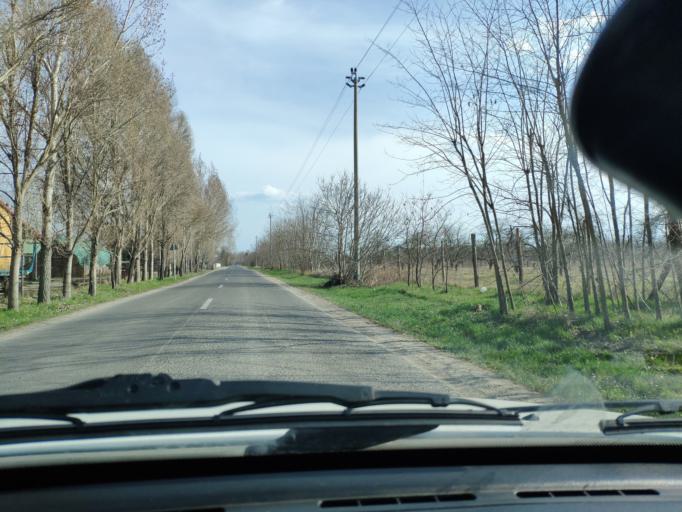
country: HU
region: Pest
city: Rackeve
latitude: 47.1888
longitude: 18.9325
